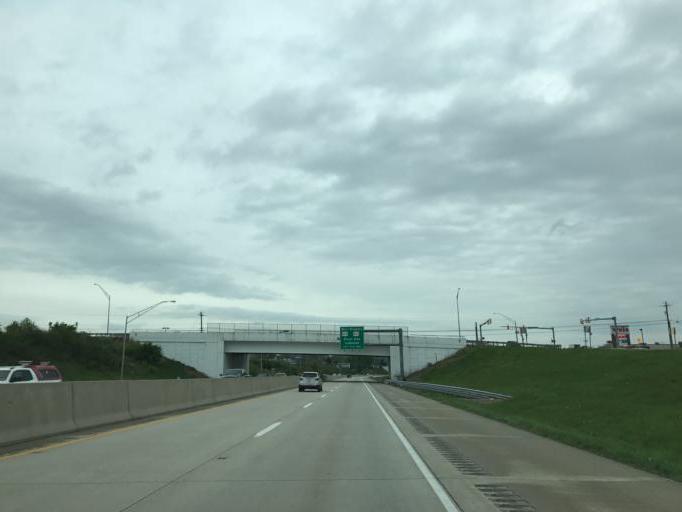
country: US
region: Pennsylvania
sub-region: Berks County
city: Montrose
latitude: 40.3129
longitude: -75.9969
